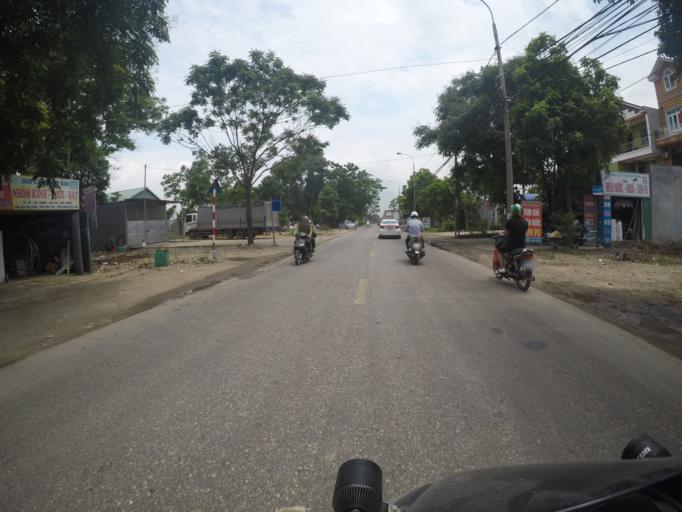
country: VN
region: Ha Noi
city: Soc Son
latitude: 21.2376
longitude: 105.8492
